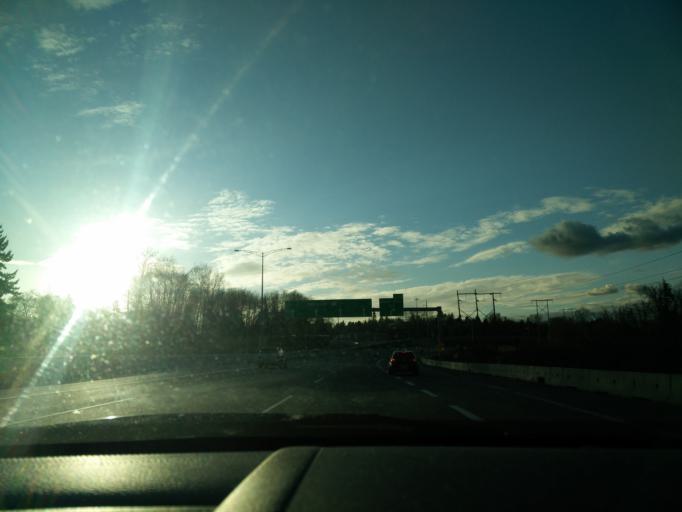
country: CA
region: British Columbia
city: Burnaby
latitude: 49.2418
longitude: -122.9619
